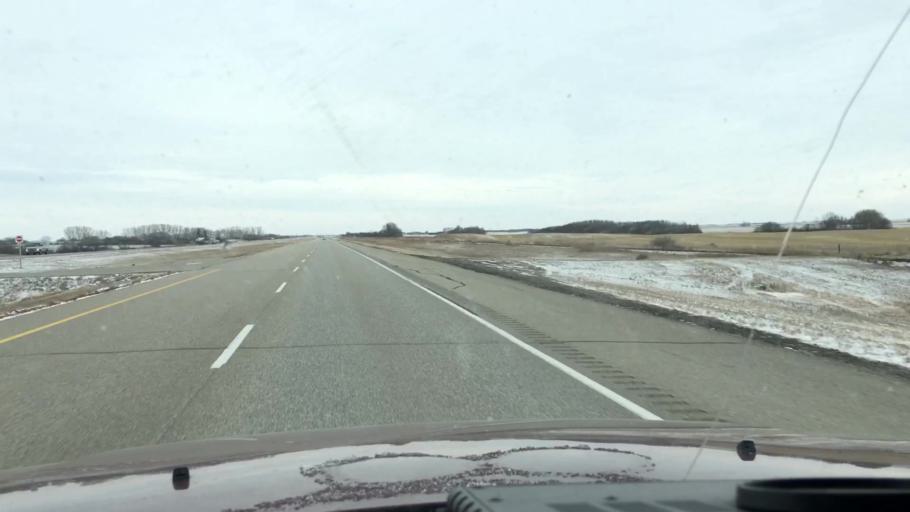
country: CA
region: Saskatchewan
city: Watrous
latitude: 51.3477
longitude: -106.1118
